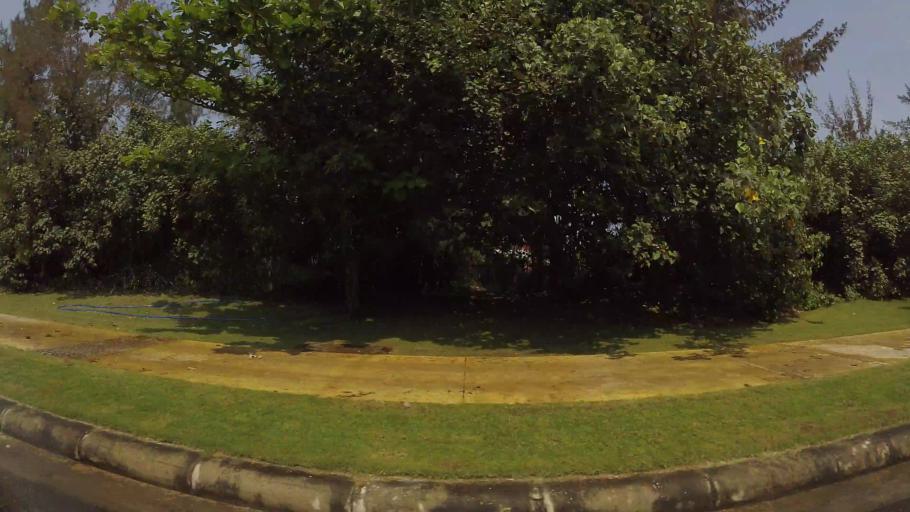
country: VN
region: Da Nang
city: Ngu Hanh Son
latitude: 15.9750
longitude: 108.2794
